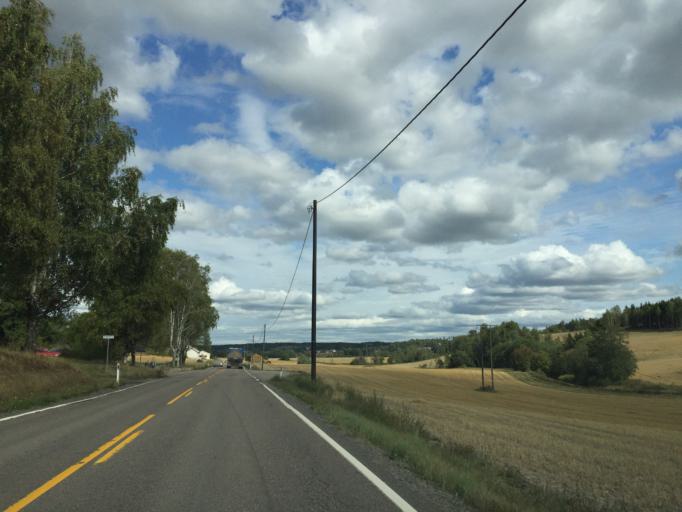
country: NO
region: Ostfold
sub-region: Hobol
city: Elvestad
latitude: 59.6107
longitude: 10.9265
